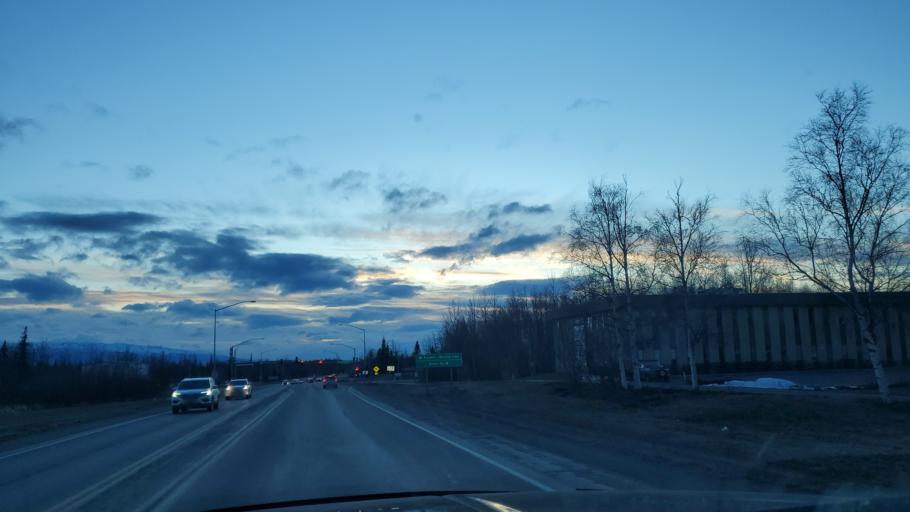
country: US
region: Alaska
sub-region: Matanuska-Susitna Borough
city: Wasilla
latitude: 61.5724
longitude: -149.4435
